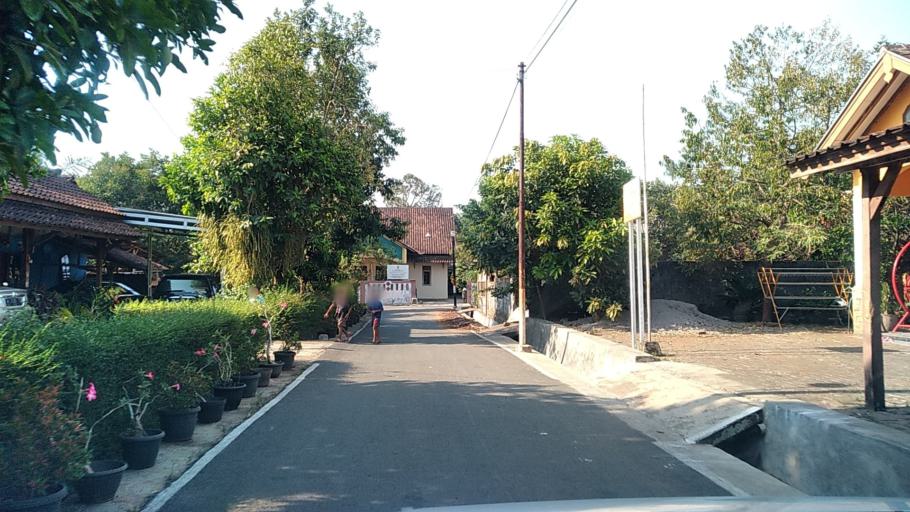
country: ID
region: Central Java
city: Ungaran
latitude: -7.0600
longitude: 110.3480
